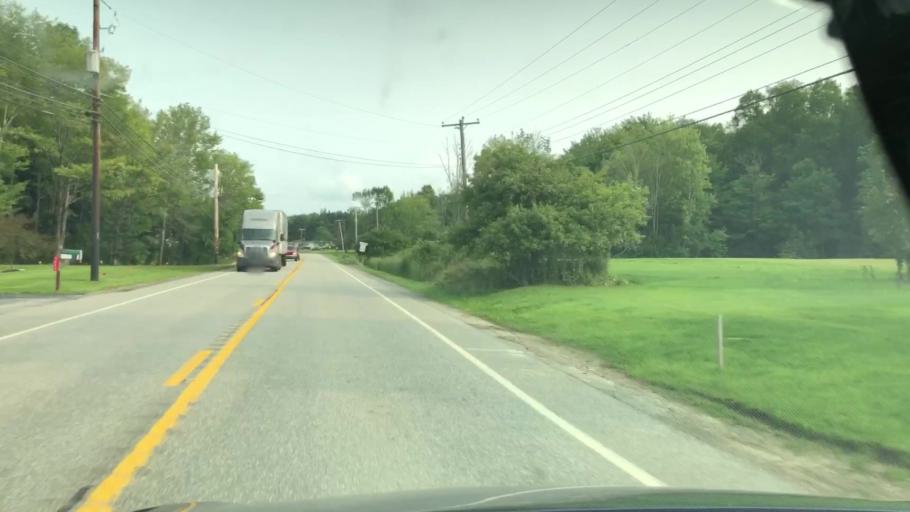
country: US
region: Pennsylvania
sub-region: Erie County
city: Wesleyville
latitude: 42.0707
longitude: -79.9828
